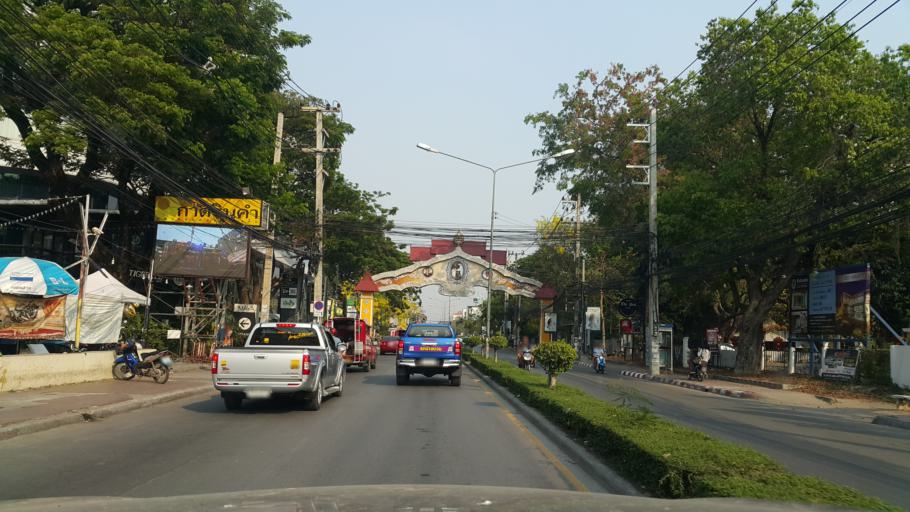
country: TH
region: Chiang Mai
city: Chiang Mai
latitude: 18.8023
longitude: 98.9661
